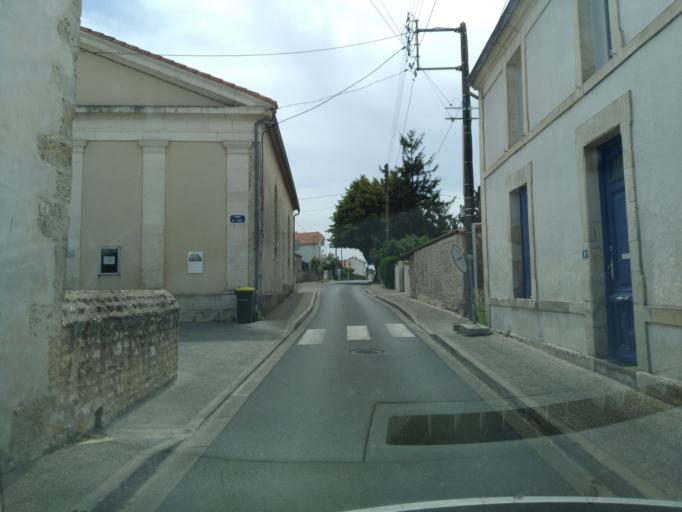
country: FR
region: Poitou-Charentes
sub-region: Departement de la Charente-Maritime
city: Saint-Palais-sur-Mer
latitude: 45.6568
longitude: -1.0770
